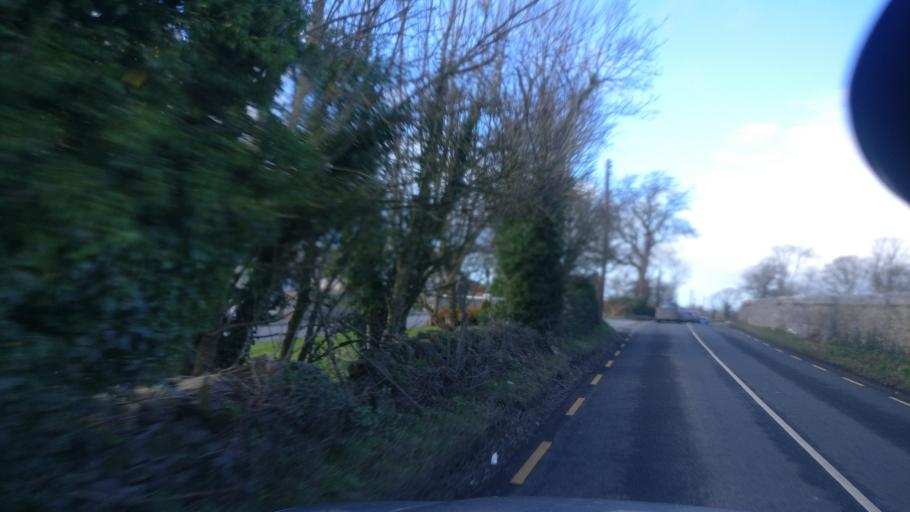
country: IE
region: Leinster
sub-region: Kilkenny
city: Kilkenny
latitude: 52.6212
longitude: -7.2088
